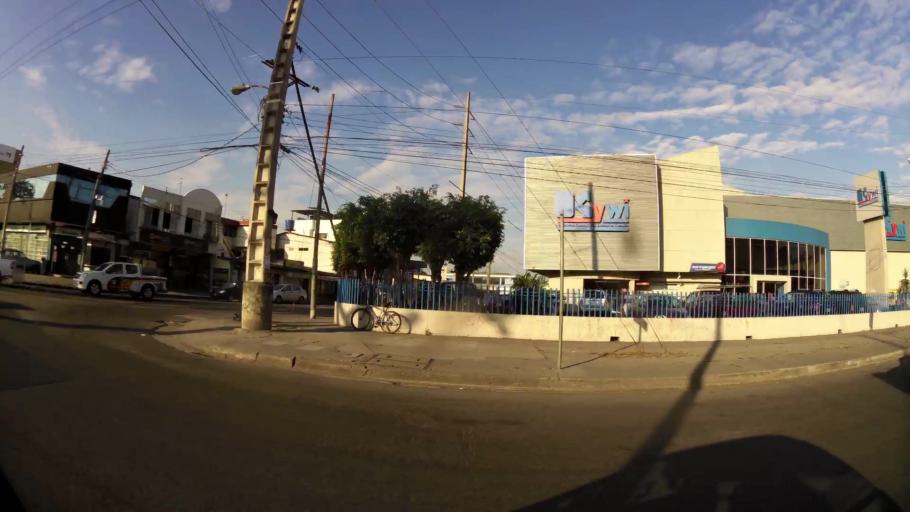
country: EC
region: Guayas
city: Guayaquil
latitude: -2.2282
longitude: -79.8977
